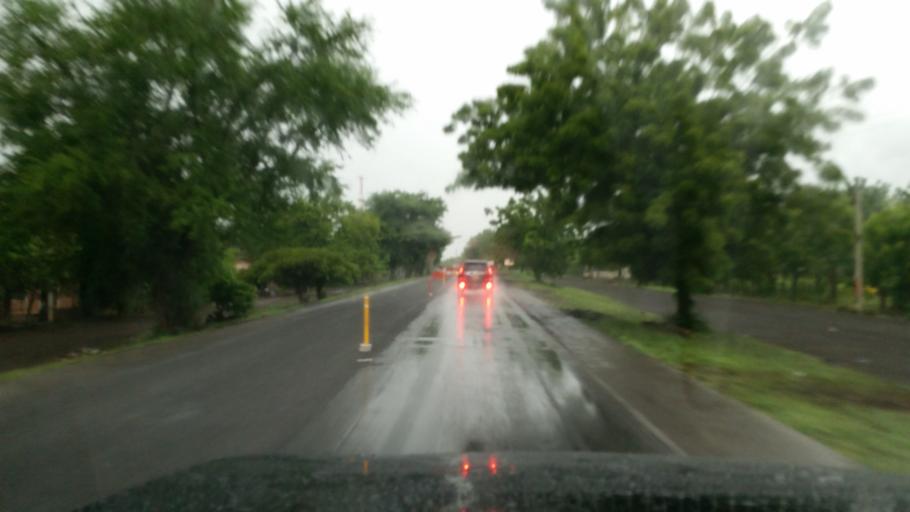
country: NI
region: Chinandega
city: Chichigalpa
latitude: 12.7875
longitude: -86.9465
